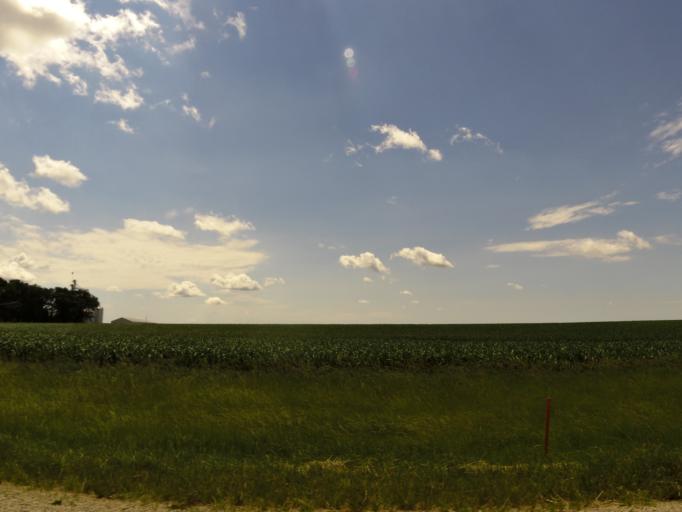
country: US
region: Iowa
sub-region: Buchanan County
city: Fairbank
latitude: 42.7149
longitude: -92.0037
